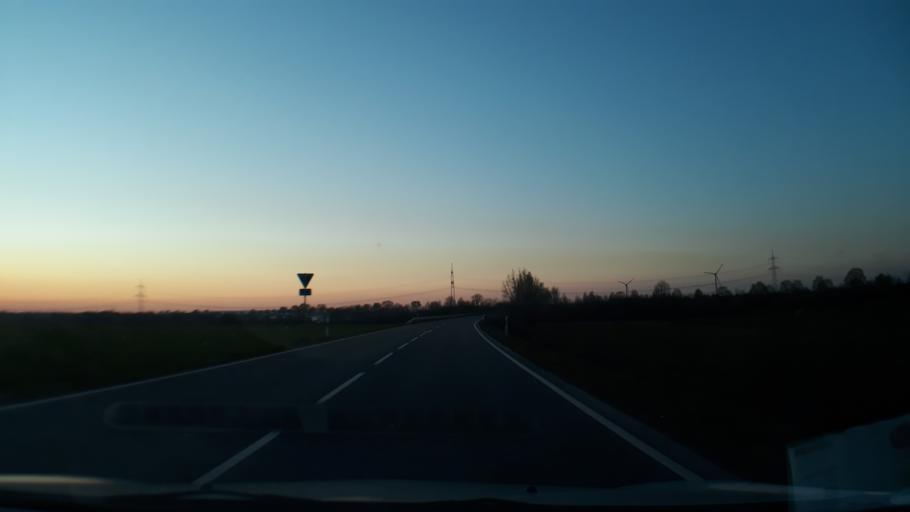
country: DE
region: North Rhine-Westphalia
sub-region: Regierungsbezirk Koln
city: Norvenich
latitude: 50.8501
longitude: 6.6151
